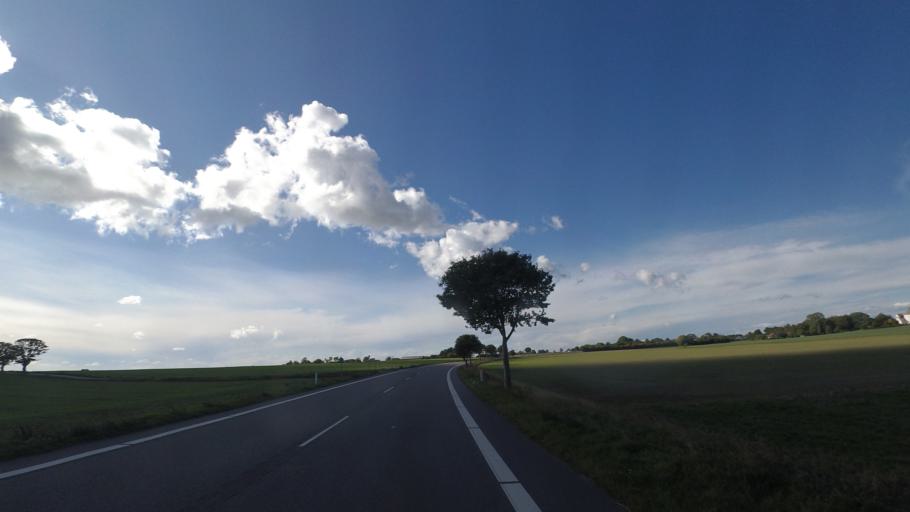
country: DK
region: Capital Region
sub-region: Bornholm Kommune
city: Akirkeby
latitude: 55.0698
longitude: 14.8227
